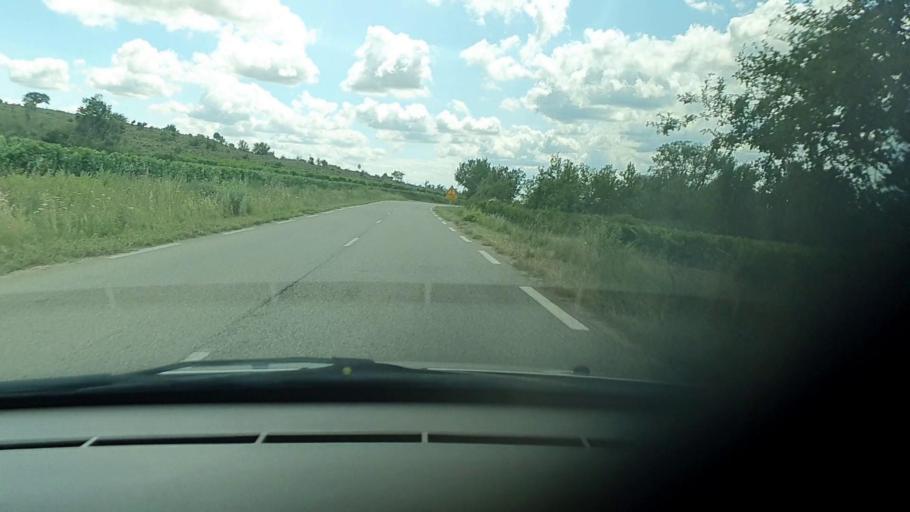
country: FR
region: Languedoc-Roussillon
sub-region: Departement du Gard
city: Moussac
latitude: 44.0110
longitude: 4.2301
